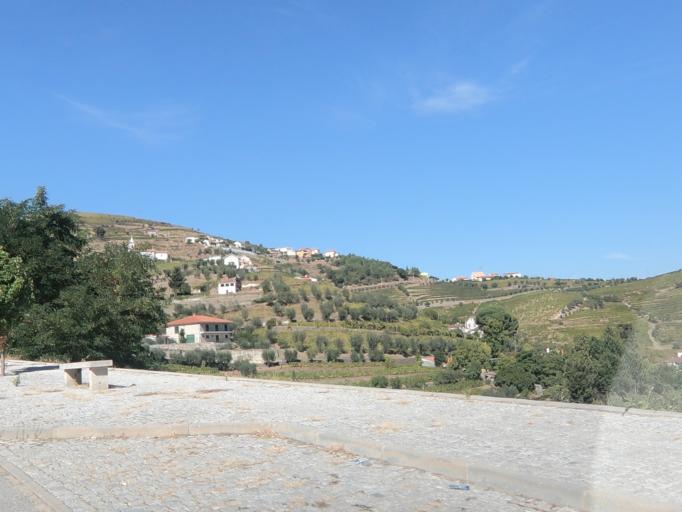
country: PT
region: Vila Real
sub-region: Santa Marta de Penaguiao
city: Santa Marta de Penaguiao
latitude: 41.2164
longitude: -7.7849
